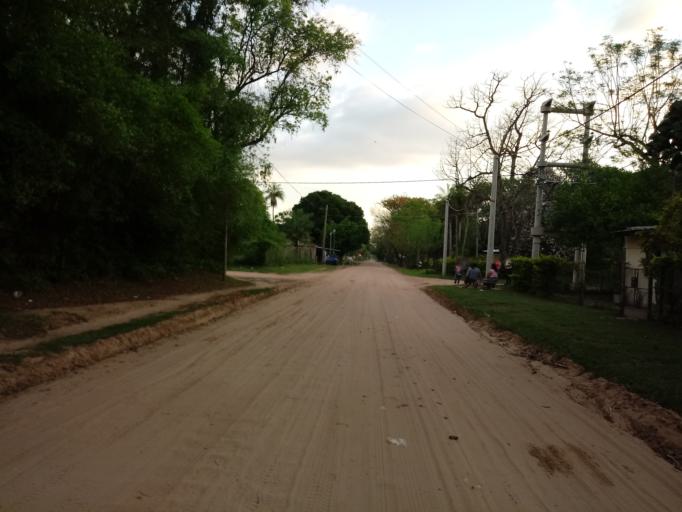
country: AR
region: Corrientes
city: San Luis del Palmar
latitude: -27.4521
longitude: -58.6548
